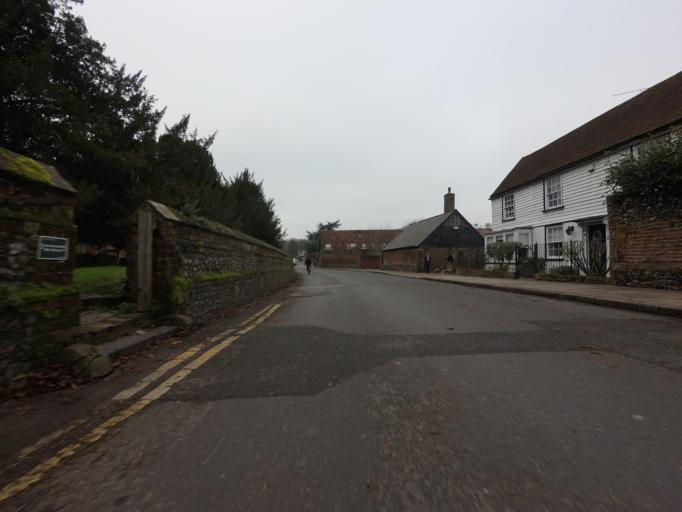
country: GB
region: England
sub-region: Kent
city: Eynsford
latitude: 51.3801
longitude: 0.2225
